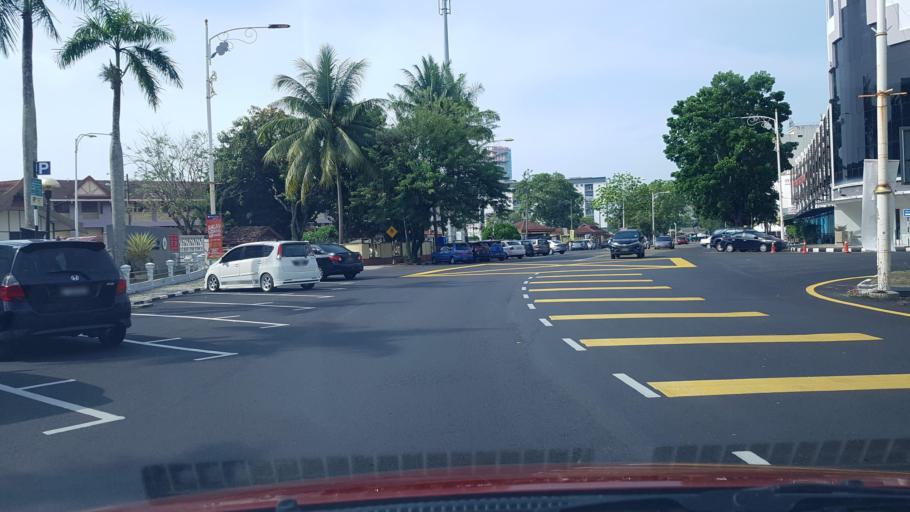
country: MY
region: Terengganu
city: Kuala Terengganu
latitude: 5.3301
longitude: 103.1416
